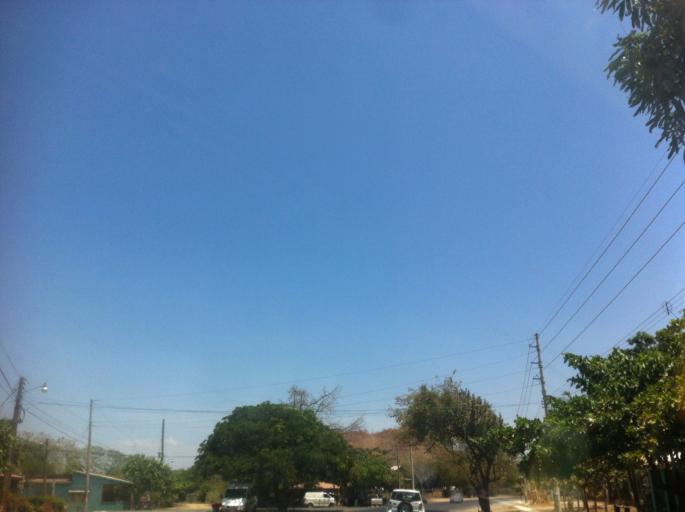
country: CR
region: Guanacaste
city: Belen
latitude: 10.4010
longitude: -85.5870
